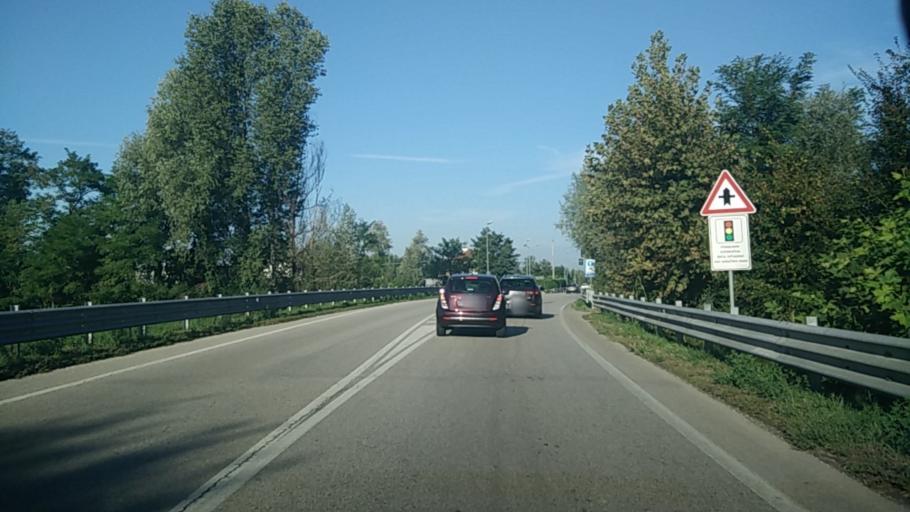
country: IT
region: Veneto
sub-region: Provincia di Padova
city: Piombino Dese
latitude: 45.6148
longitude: 12.0000
